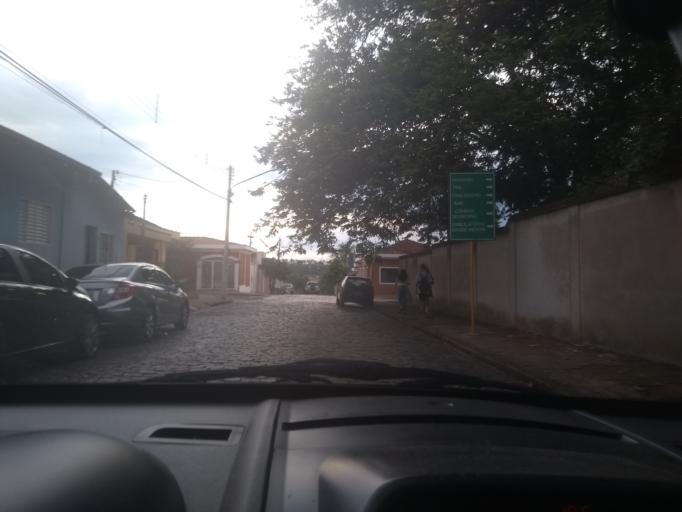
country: BR
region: Sao Paulo
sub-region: Casa Branca
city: Casa Branca
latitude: -21.7773
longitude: -47.0831
